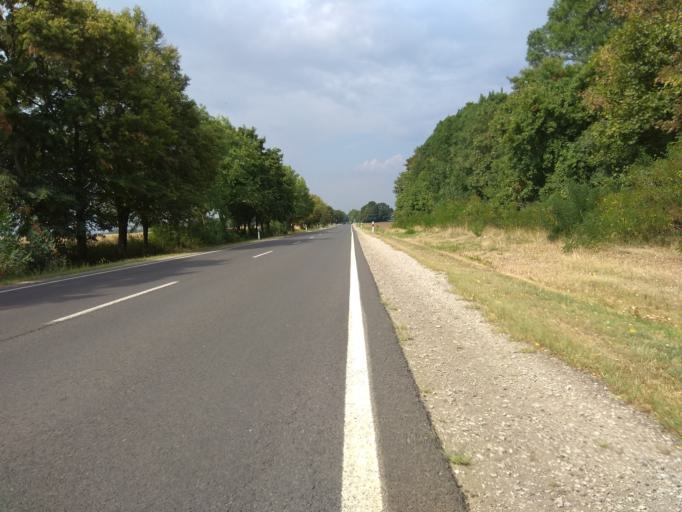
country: HU
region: Borsod-Abauj-Zemplen
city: Emod
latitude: 47.9291
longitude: 20.7942
